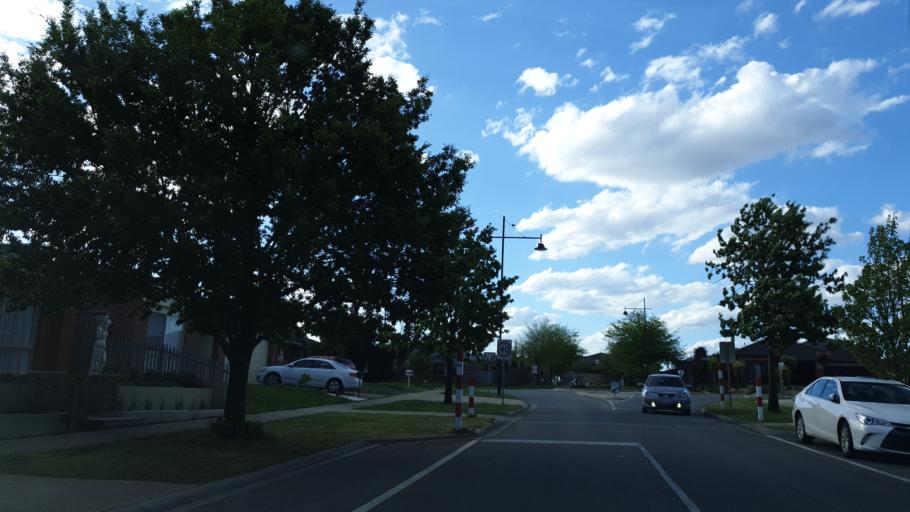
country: AU
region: Victoria
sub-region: Casey
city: Cranbourne North
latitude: -38.0872
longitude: 145.2881
